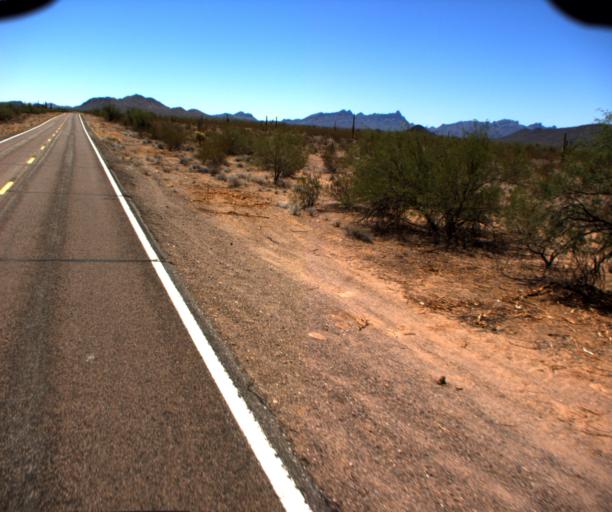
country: US
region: Arizona
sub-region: Pima County
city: Ajo
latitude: 32.2407
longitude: -112.7239
